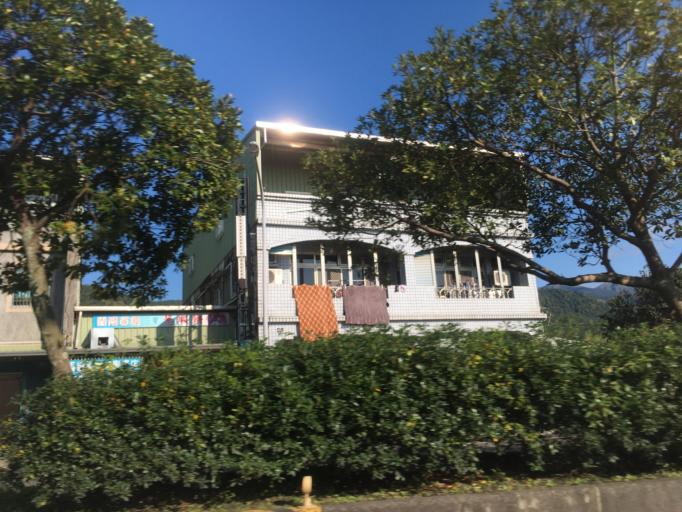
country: TW
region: Taiwan
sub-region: Yilan
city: Yilan
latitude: 24.8388
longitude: 121.7944
